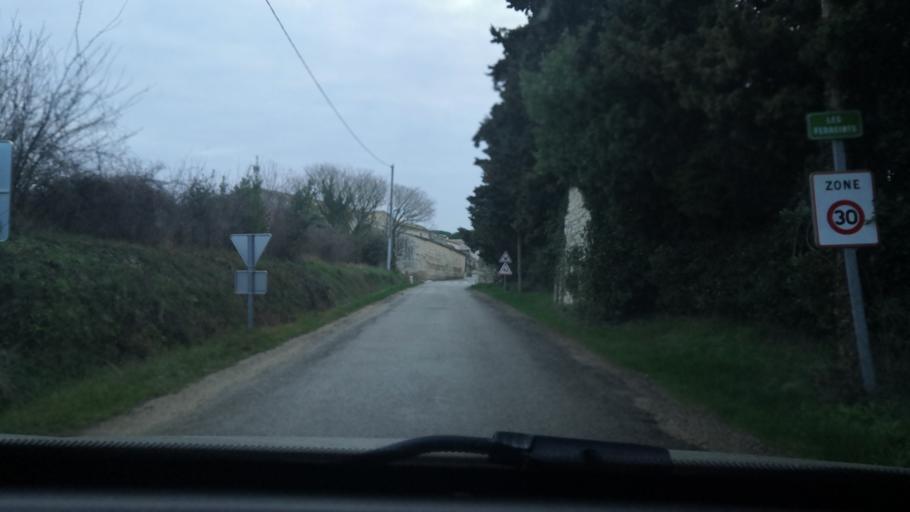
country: FR
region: Rhone-Alpes
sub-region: Departement de la Drome
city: Allan
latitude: 44.5151
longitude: 4.7926
